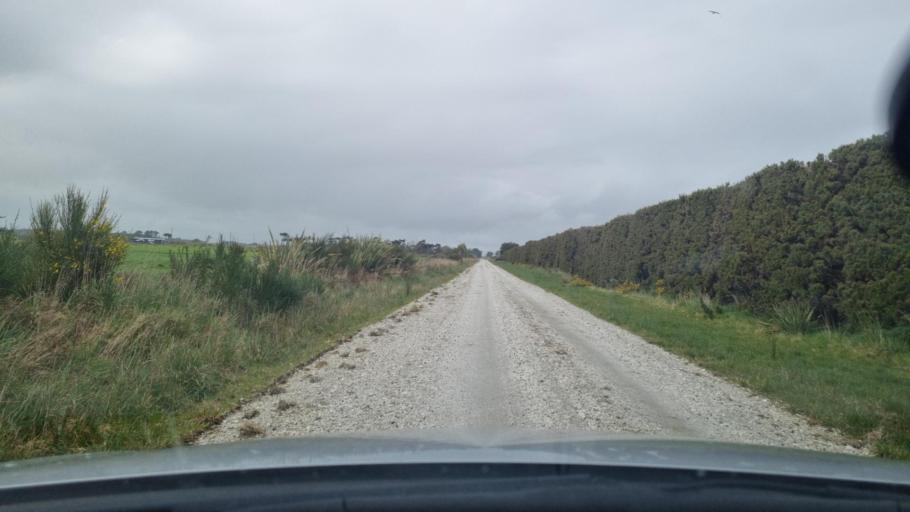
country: NZ
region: Southland
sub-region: Invercargill City
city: Invercargill
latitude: -46.4983
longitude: 168.4143
